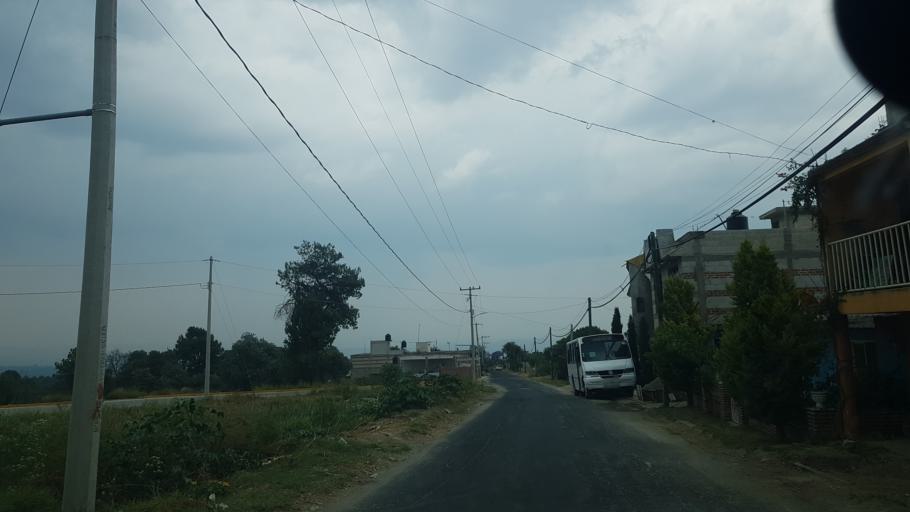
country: MX
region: Puebla
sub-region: Chiautzingo
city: San Nicolas Zecalacoayan
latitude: 19.1781
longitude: -98.4882
